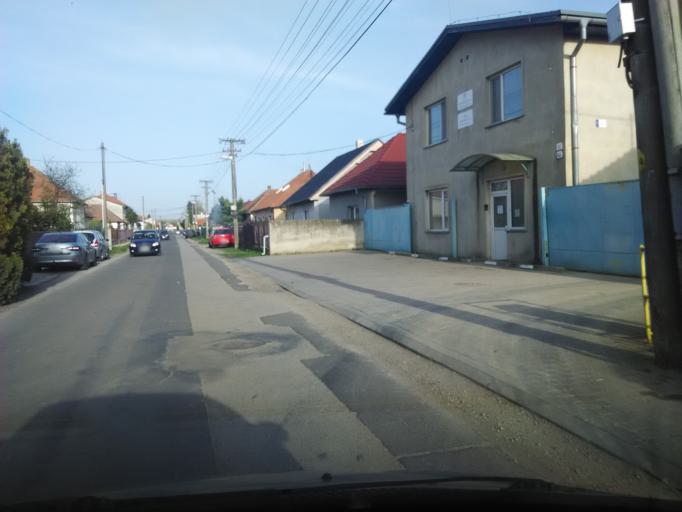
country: SK
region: Nitriansky
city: Surany
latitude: 48.0487
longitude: 18.1789
